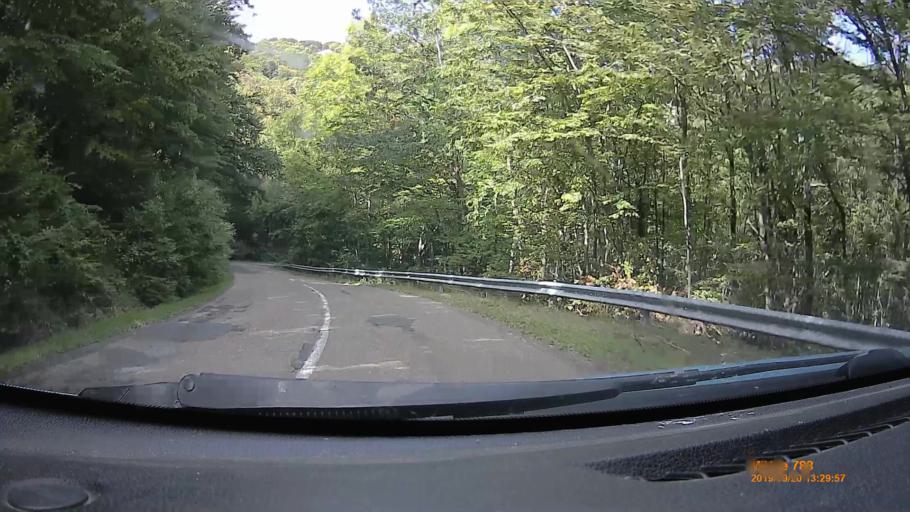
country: HU
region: Heves
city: Szilvasvarad
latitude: 48.0560
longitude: 20.4841
